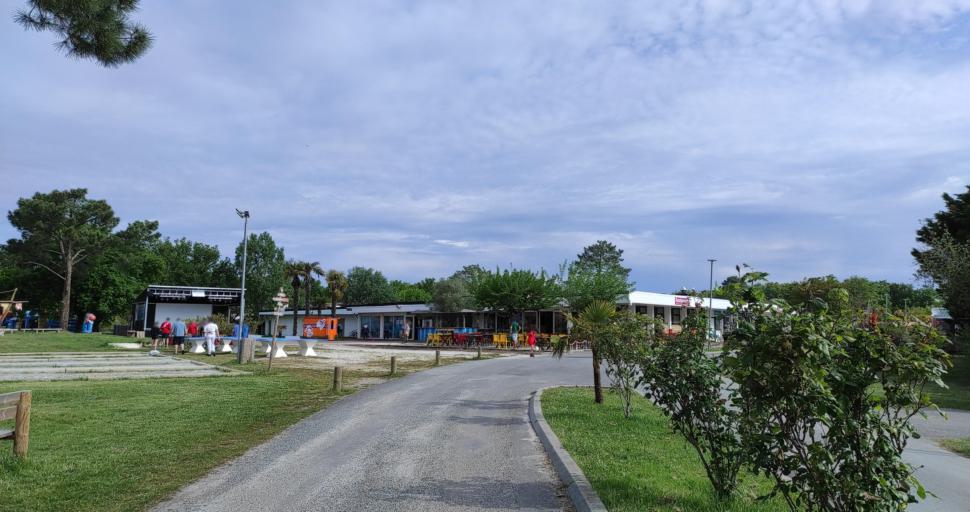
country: FR
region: Aquitaine
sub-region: Departement de la Gironde
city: Lanton
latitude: 44.7035
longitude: -1.0491
